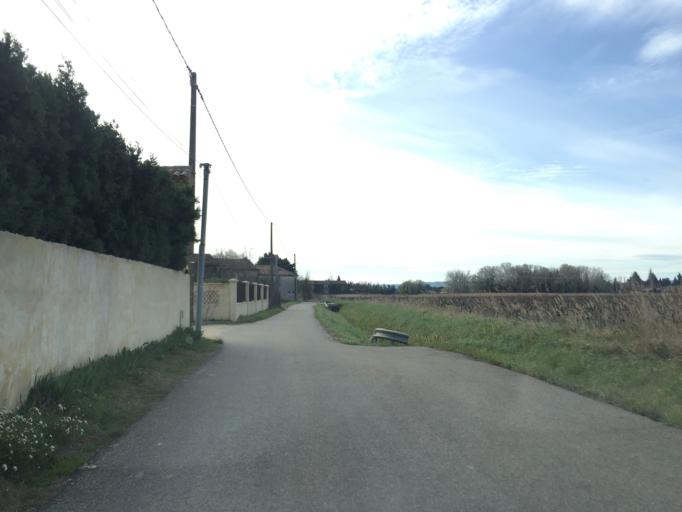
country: FR
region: Provence-Alpes-Cote d'Azur
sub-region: Departement du Vaucluse
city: Caderousse
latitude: 44.1204
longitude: 4.7469
